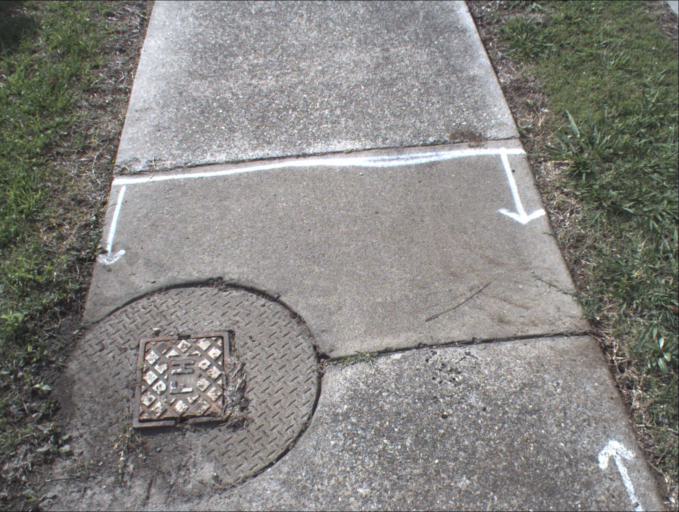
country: AU
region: Queensland
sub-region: Logan
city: Waterford West
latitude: -27.6902
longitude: 153.1296
